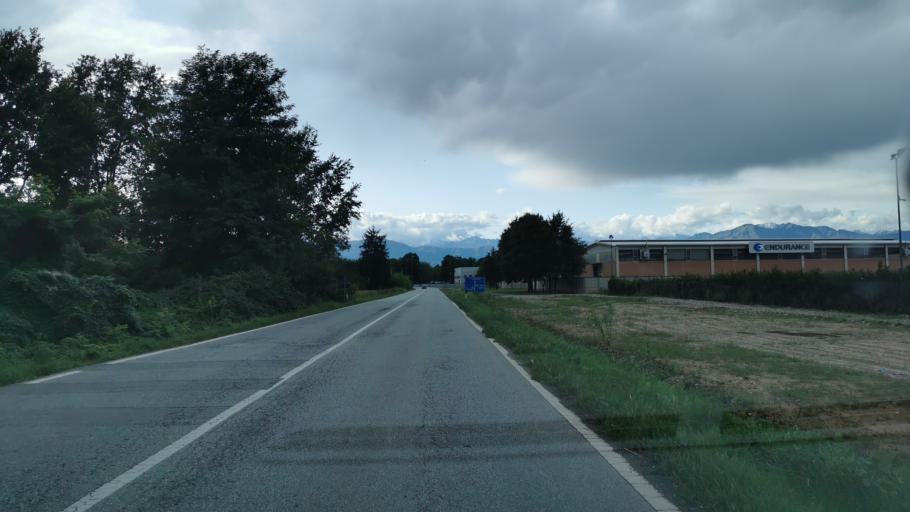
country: IT
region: Piedmont
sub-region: Provincia di Torino
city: Lombardore
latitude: 45.2295
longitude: 7.7532
